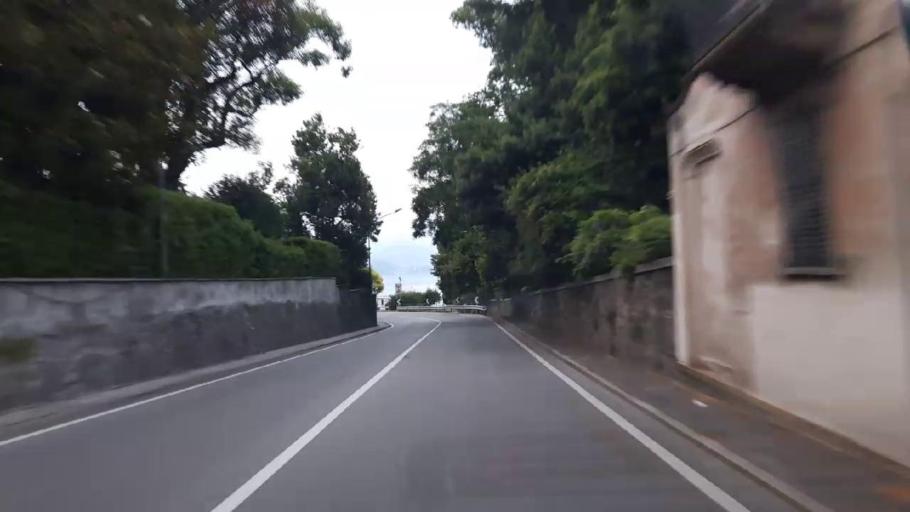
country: IT
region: Piedmont
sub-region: Provincia di Novara
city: Lesa
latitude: 45.8274
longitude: 8.5652
